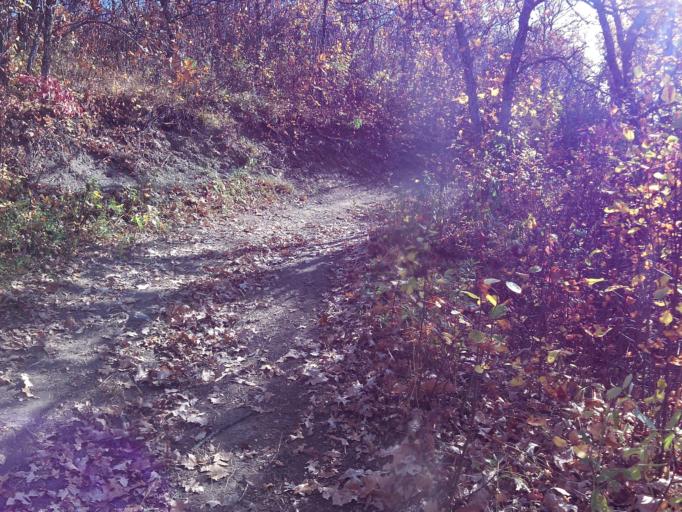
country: CA
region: Manitoba
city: Morden
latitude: 48.9484
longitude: -98.0683
